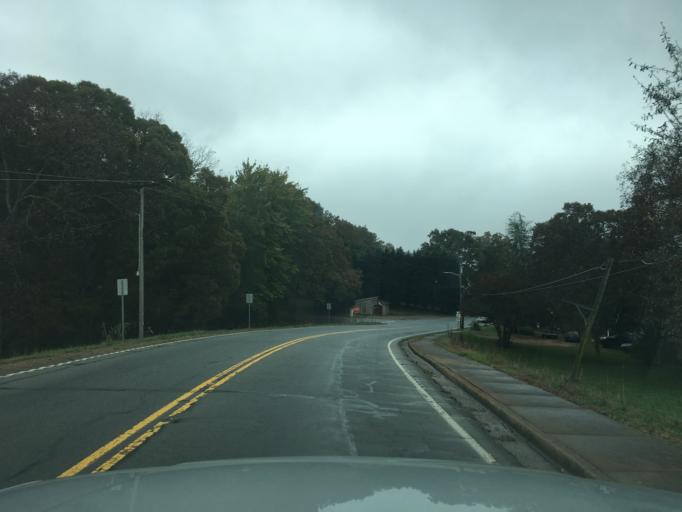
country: US
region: South Carolina
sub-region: Pickens County
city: Central
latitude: 34.7635
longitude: -82.7525
